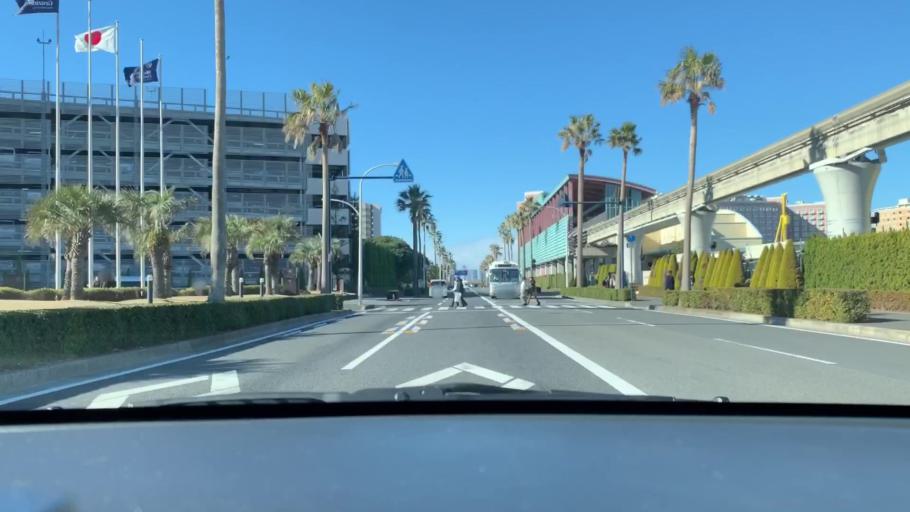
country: JP
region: Tokyo
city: Urayasu
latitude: 35.6274
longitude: 139.8778
